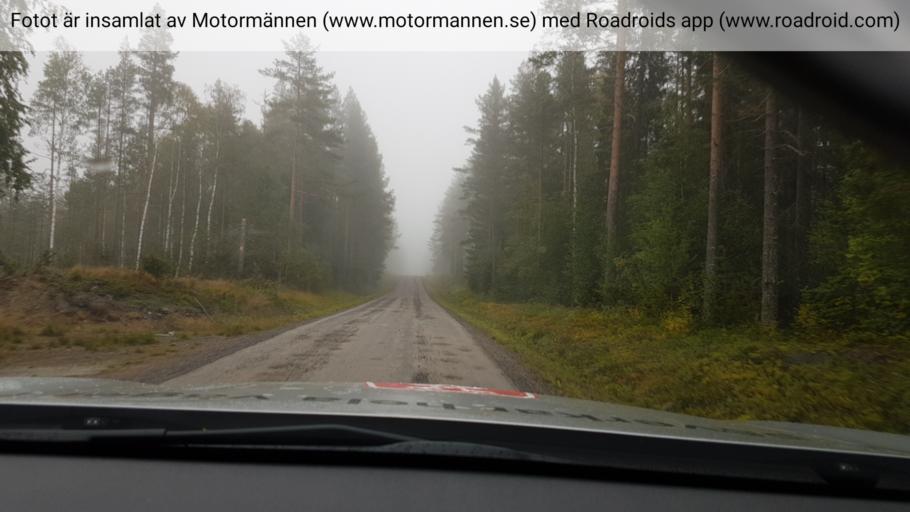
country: SE
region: Vaesterbotten
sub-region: Umea Kommun
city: Ersmark
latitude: 64.1098
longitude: 20.3378
